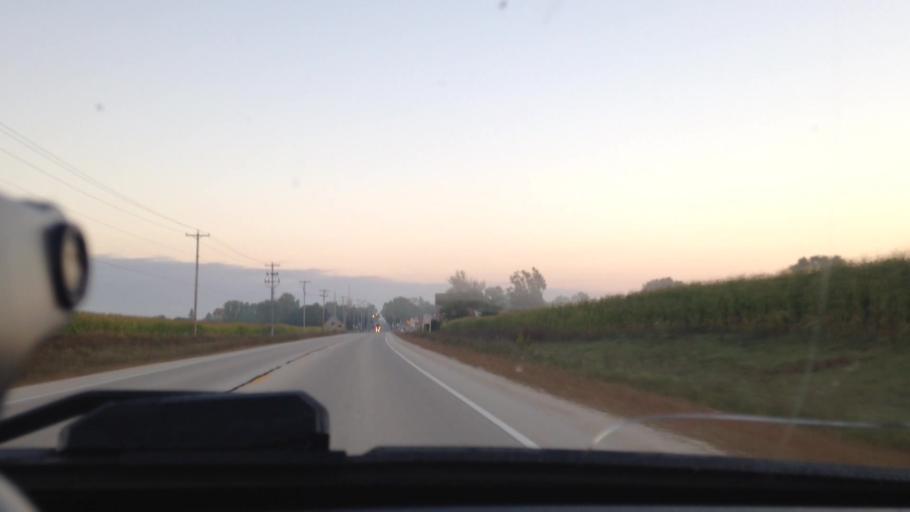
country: US
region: Wisconsin
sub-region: Dodge County
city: Lomira
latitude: 43.5824
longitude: -88.4500
